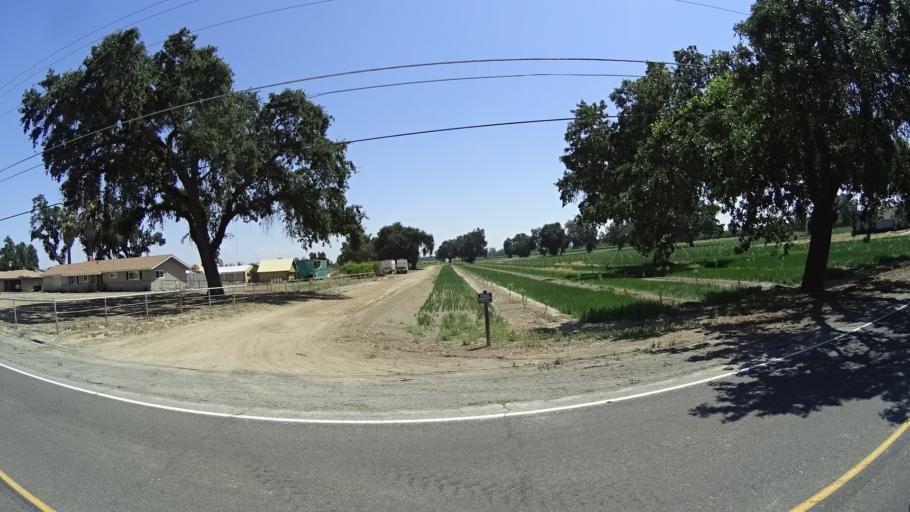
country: US
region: California
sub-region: Fresno County
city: Laton
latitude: 36.4219
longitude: -119.6864
